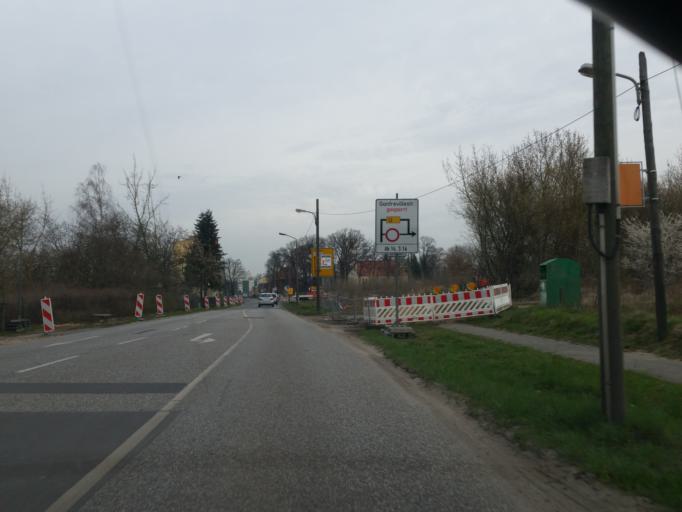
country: DE
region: Brandenburg
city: Teltow
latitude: 52.3944
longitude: 13.2669
